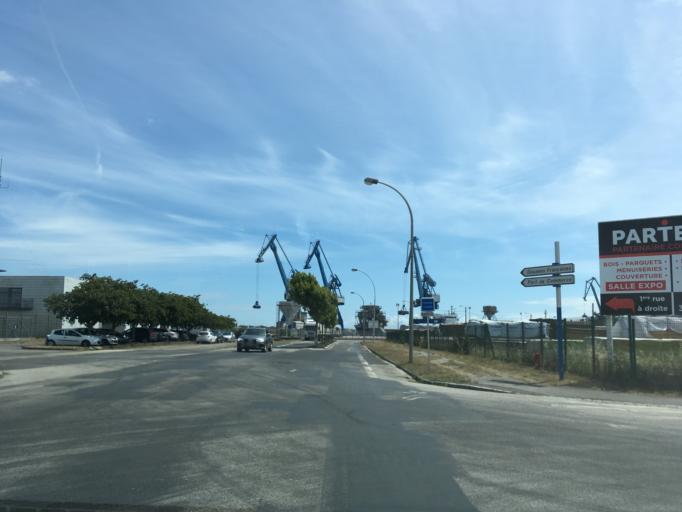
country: FR
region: Brittany
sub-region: Departement du Morbihan
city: Lorient
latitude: 47.7393
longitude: -3.3565
